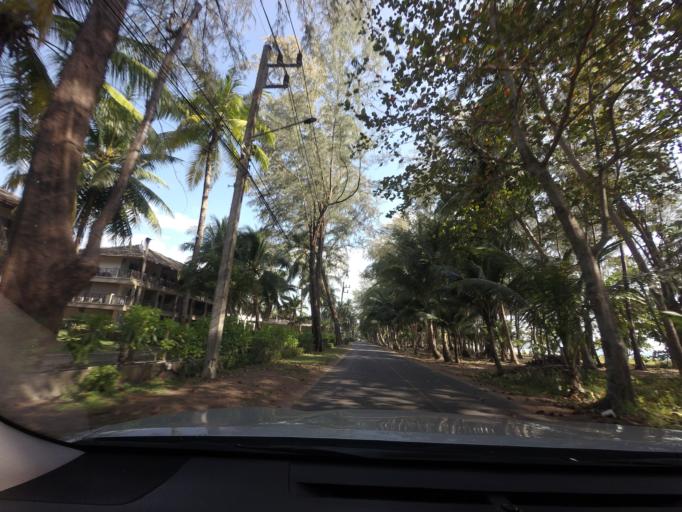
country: TH
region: Phangnga
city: Ban Khao Lak
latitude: 8.7247
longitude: 98.2309
